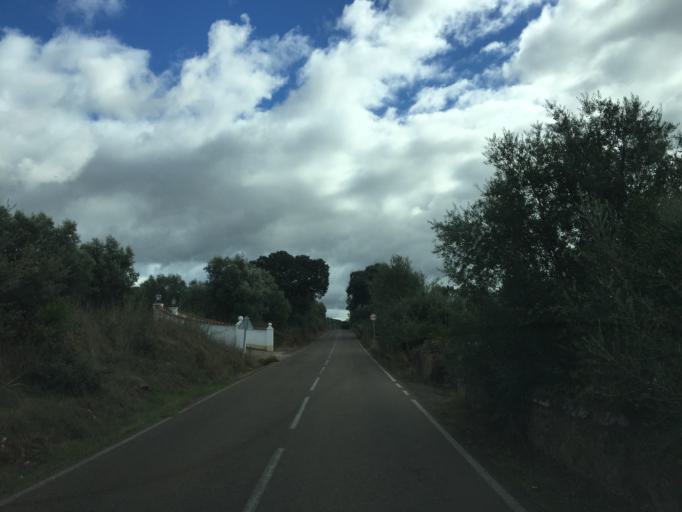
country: PT
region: Portalegre
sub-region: Alter do Chao
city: Alter do Chao
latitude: 39.2167
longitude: -7.6695
